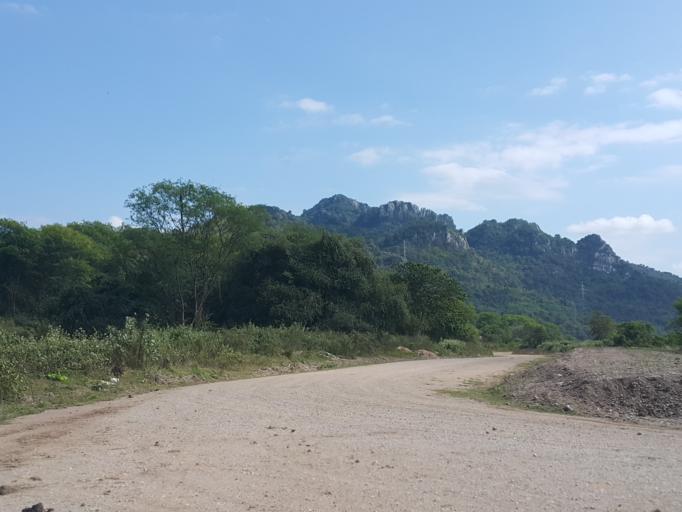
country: TH
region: Lampang
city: Mae Mo
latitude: 18.3324
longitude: 99.7553
